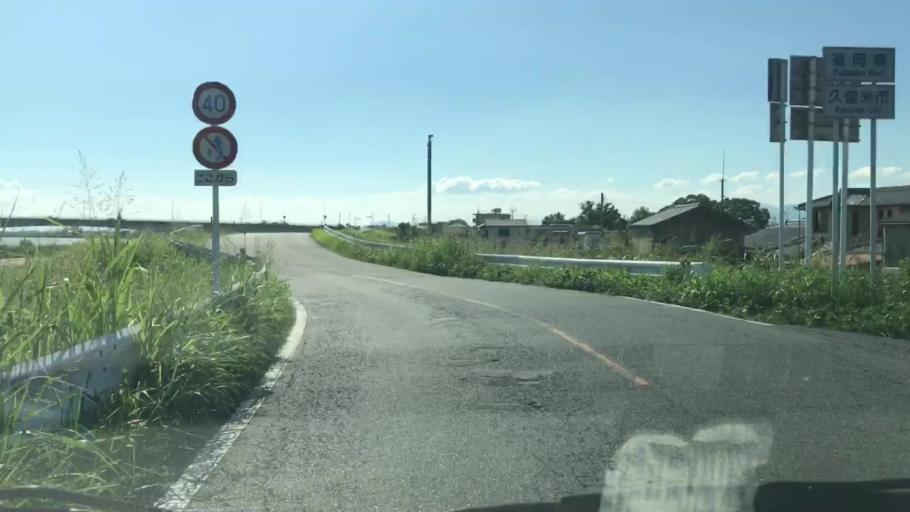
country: JP
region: Saga Prefecture
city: Kanzakimachi-kanzaki
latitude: 33.2731
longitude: 130.4356
